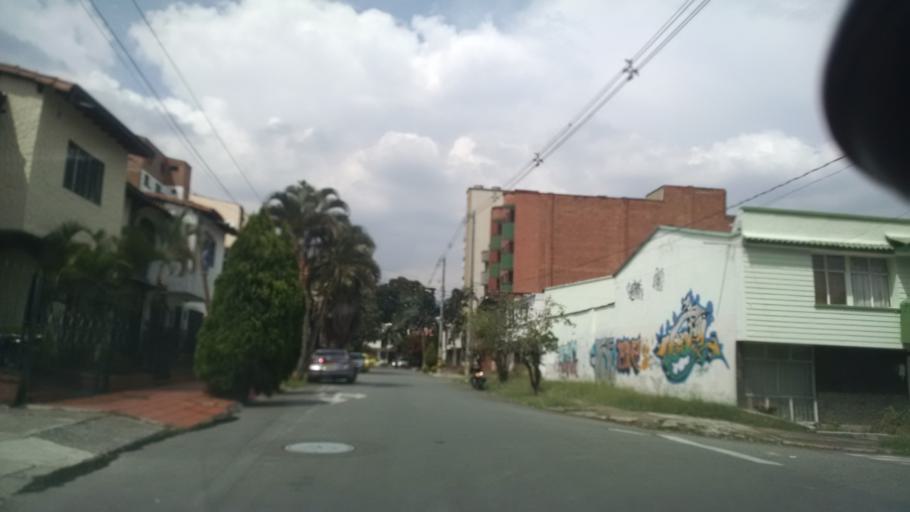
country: CO
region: Antioquia
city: Medellin
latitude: 6.2410
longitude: -75.6024
